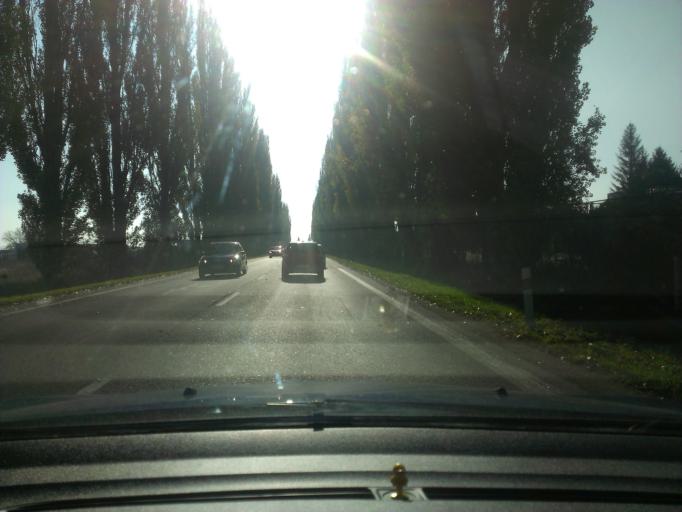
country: SK
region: Nitriansky
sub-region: Okres Nitra
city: Nitra
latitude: 48.2627
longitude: 18.1044
